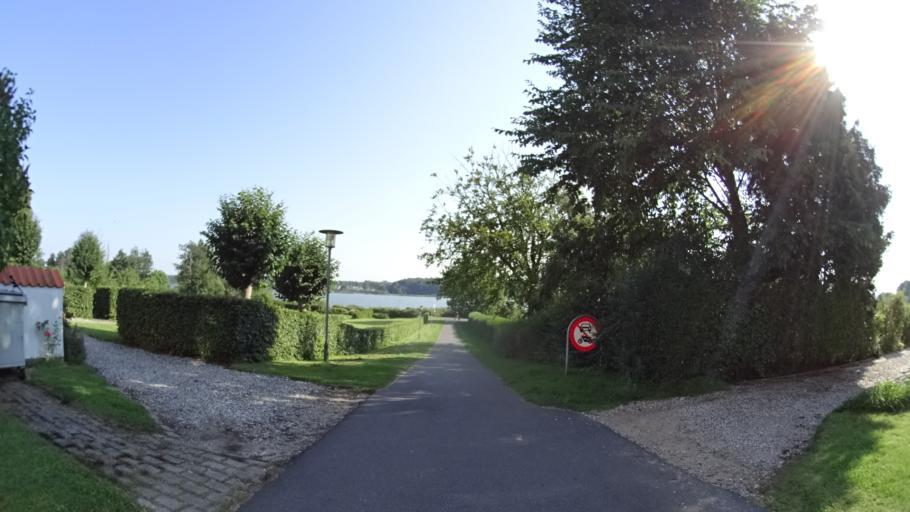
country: DK
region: Central Jutland
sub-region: Arhus Kommune
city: Stavtrup
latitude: 56.1513
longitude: 10.1045
